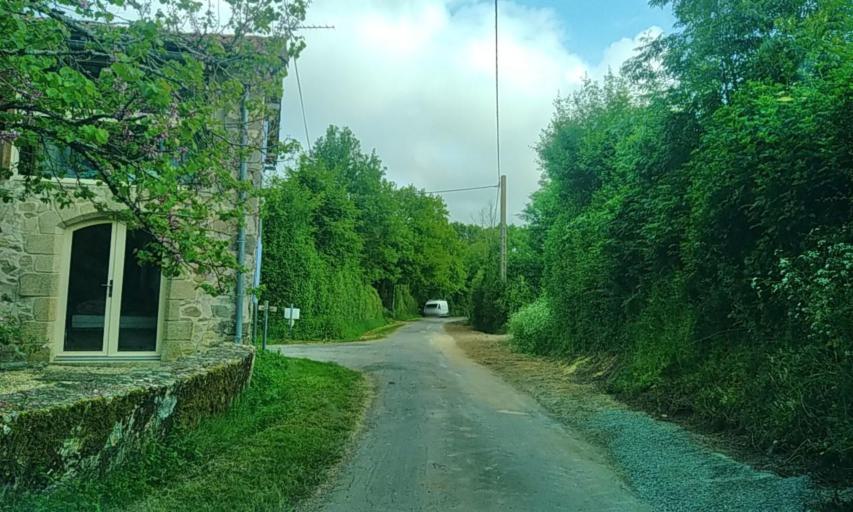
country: FR
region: Poitou-Charentes
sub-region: Departement des Deux-Sevres
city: Boisme
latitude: 46.7595
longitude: -0.4357
